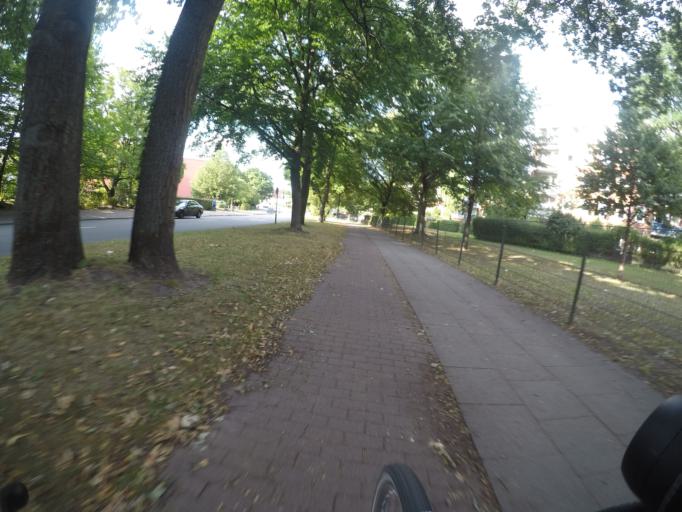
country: DE
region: Schleswig-Holstein
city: Barsbuettel
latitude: 53.5825
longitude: 10.1405
